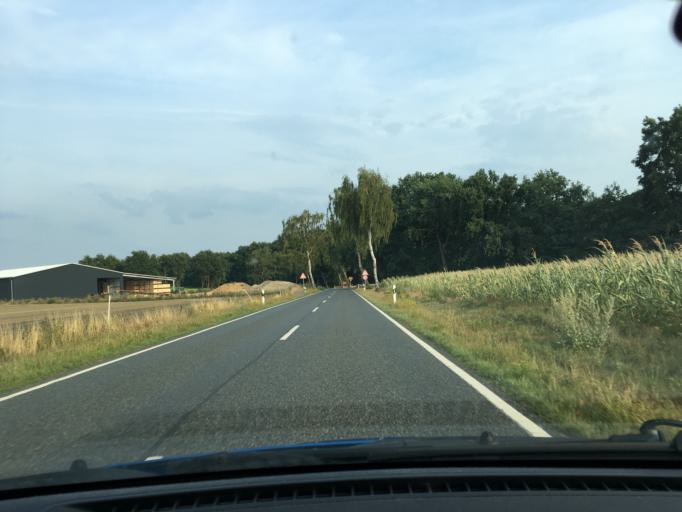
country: DE
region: Lower Saxony
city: Toppenstedt
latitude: 53.3033
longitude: 10.0889
